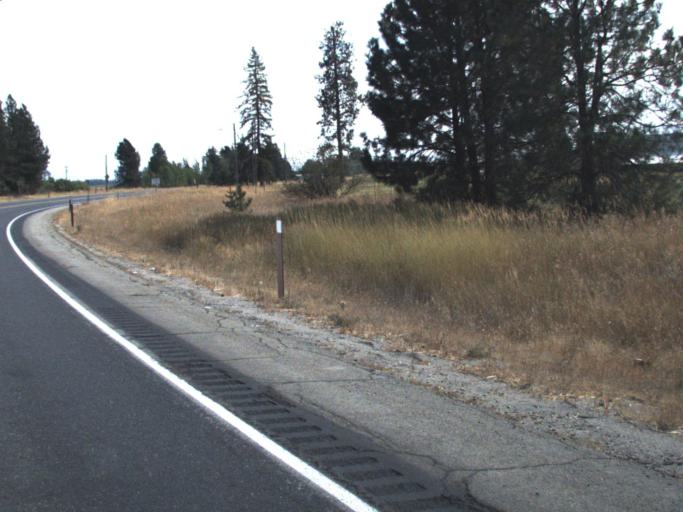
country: US
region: Washington
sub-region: Spokane County
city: Deer Park
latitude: 47.9934
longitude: -117.5466
